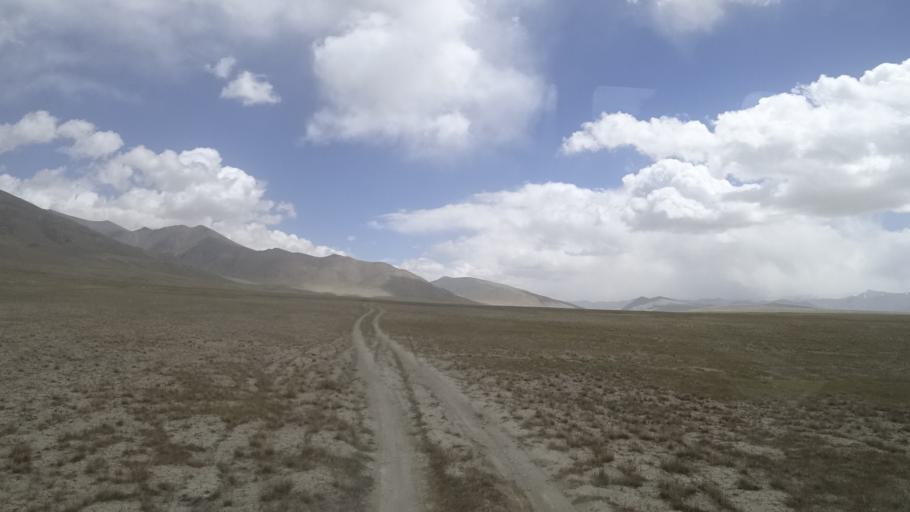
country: TJ
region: Gorno-Badakhshan
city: Murghob
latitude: 37.4850
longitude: 73.9871
